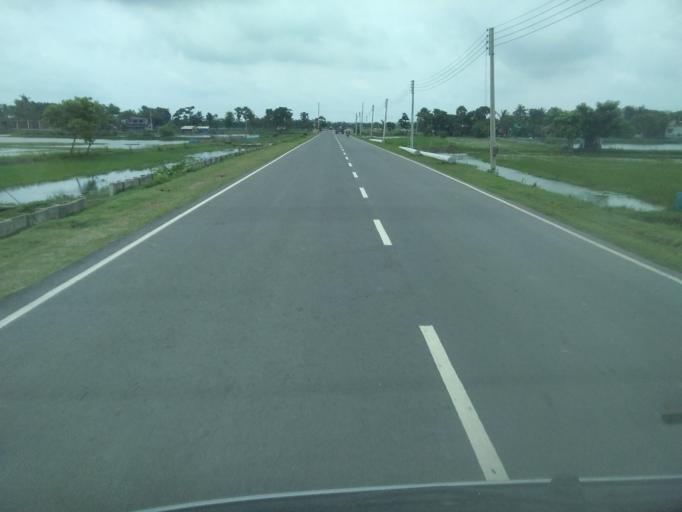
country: BD
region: Khulna
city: Satkhira
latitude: 22.7056
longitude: 89.0558
